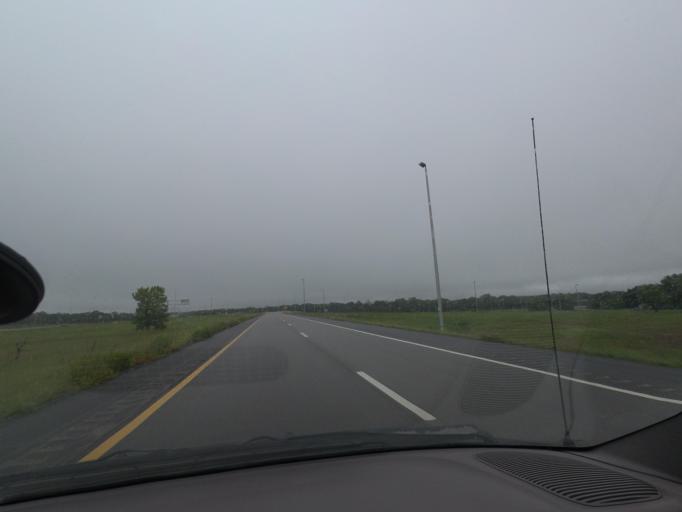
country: US
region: Illinois
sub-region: Macon County
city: Harristown
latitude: 39.8370
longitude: -89.0476
